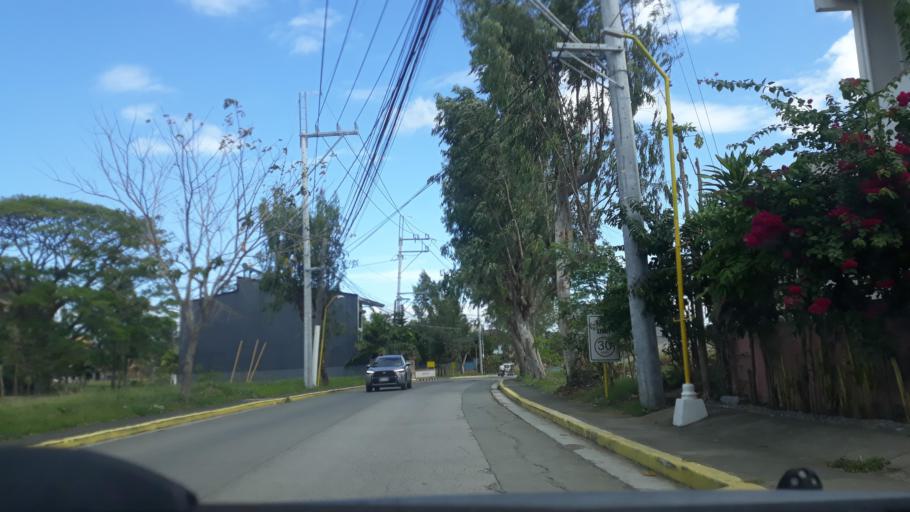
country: PH
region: Calabarzon
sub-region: Province of Cavite
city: Bulihan
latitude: 14.3012
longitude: 120.9660
